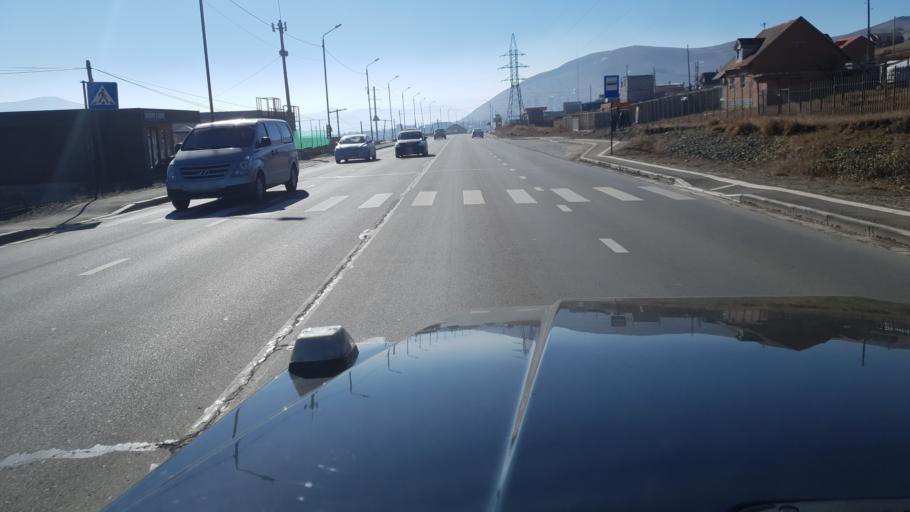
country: MN
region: Ulaanbaatar
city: Ulaanbaatar
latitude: 48.0254
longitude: 106.9132
